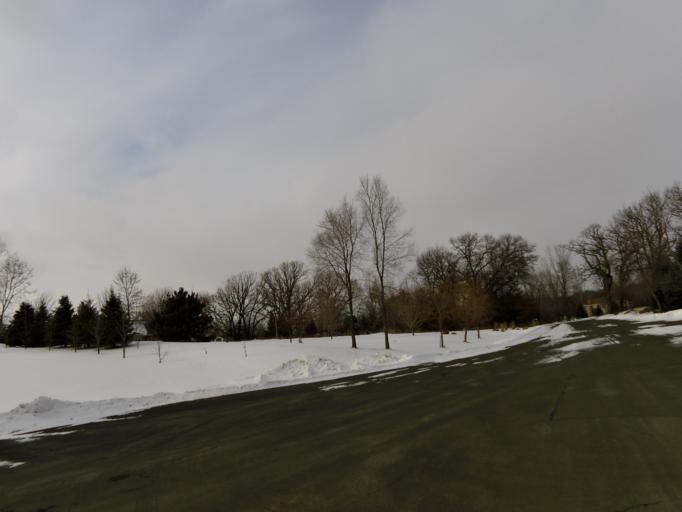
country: US
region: Minnesota
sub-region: Washington County
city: Lake Elmo
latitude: 44.9702
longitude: -92.8498
